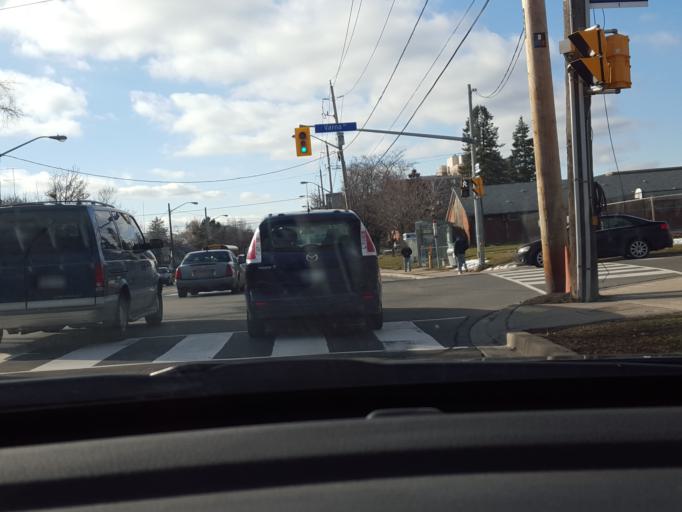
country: CA
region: Ontario
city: Toronto
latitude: 43.7176
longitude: -79.4374
